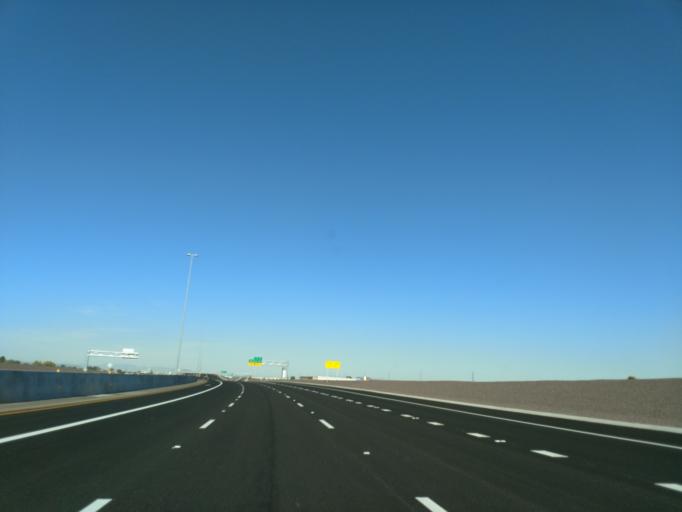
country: US
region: Arizona
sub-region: Maricopa County
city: Laveen
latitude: 33.3704
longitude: -112.1891
